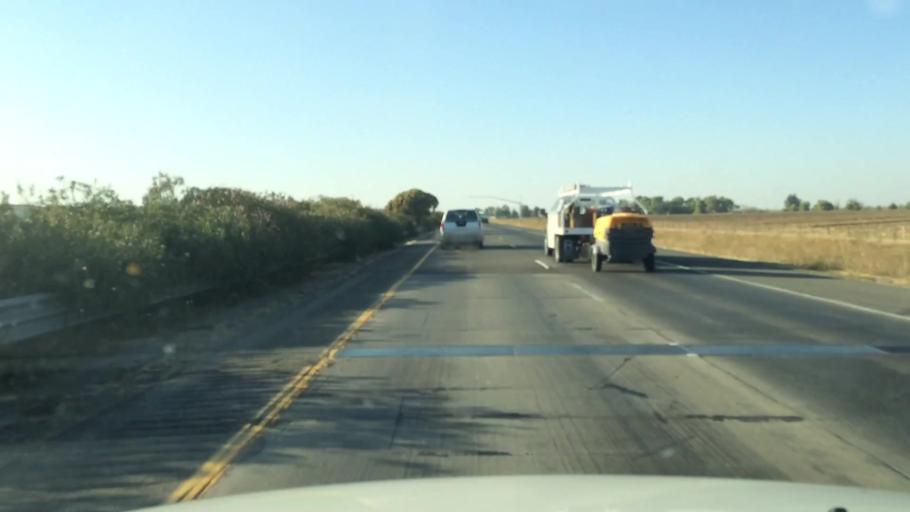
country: US
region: California
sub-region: Madera County
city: Chowchilla
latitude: 37.1457
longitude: -120.2822
